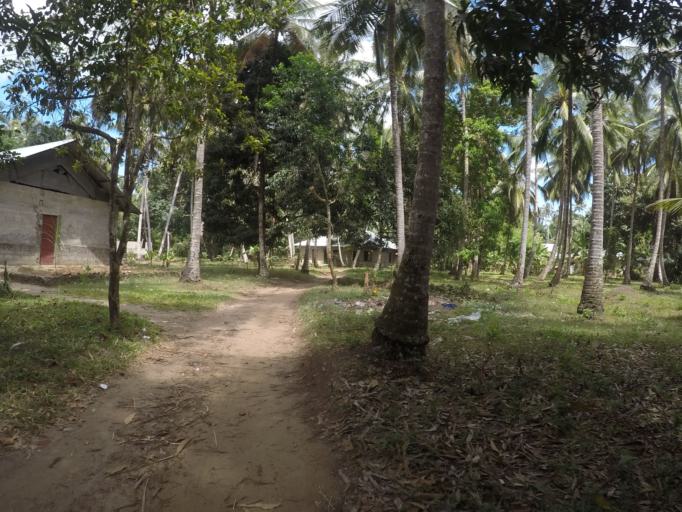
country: TZ
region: Zanzibar Urban/West
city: Zanzibar
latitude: -6.2056
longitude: 39.2379
